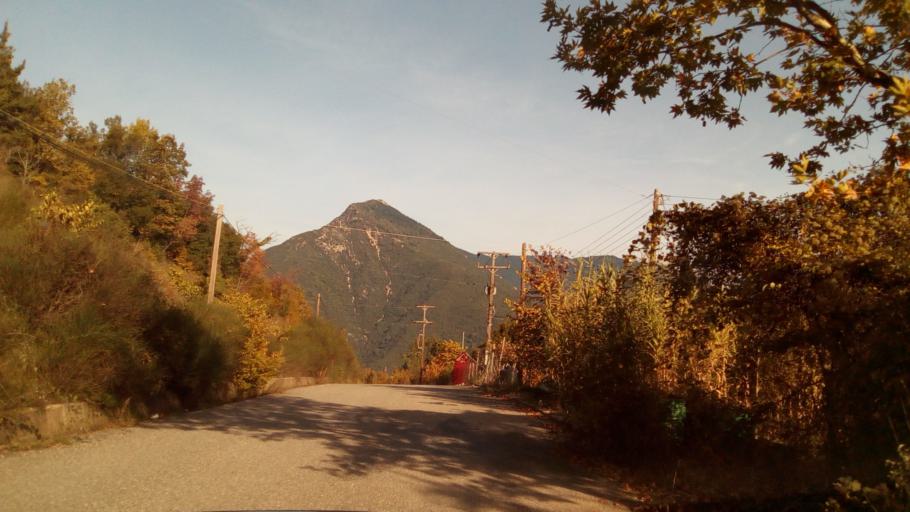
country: GR
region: West Greece
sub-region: Nomos Aitolias kai Akarnanias
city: Thermo
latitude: 38.6555
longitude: 21.8445
